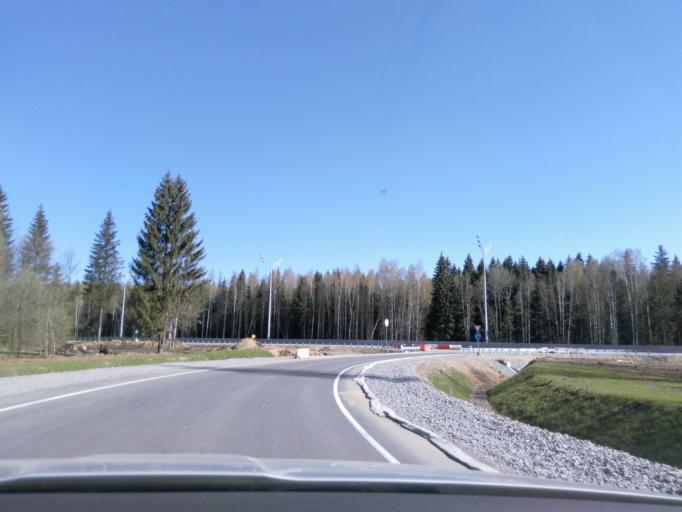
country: RU
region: Moskovskaya
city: Mendeleyevo
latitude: 56.0642
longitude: 37.2313
